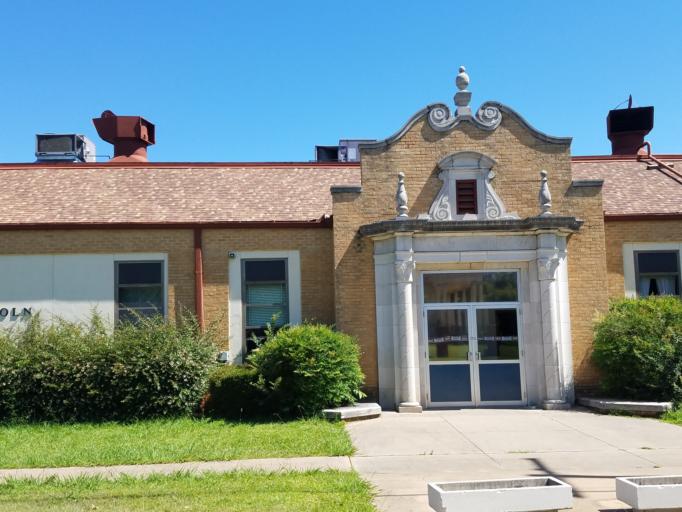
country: US
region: Oklahoma
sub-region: Carter County
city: Ardmore
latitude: 34.1712
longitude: -97.1391
